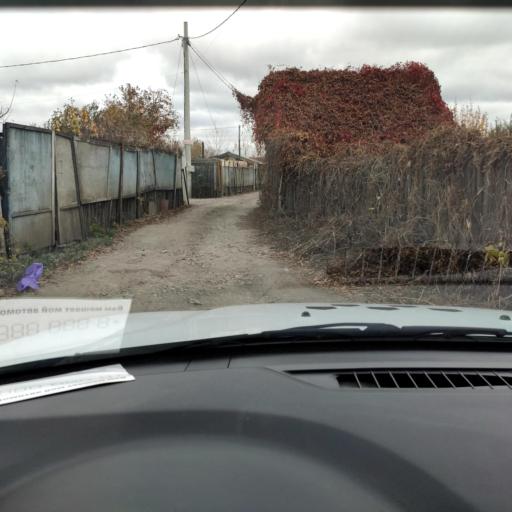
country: RU
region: Samara
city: Tol'yatti
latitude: 53.5376
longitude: 49.4307
